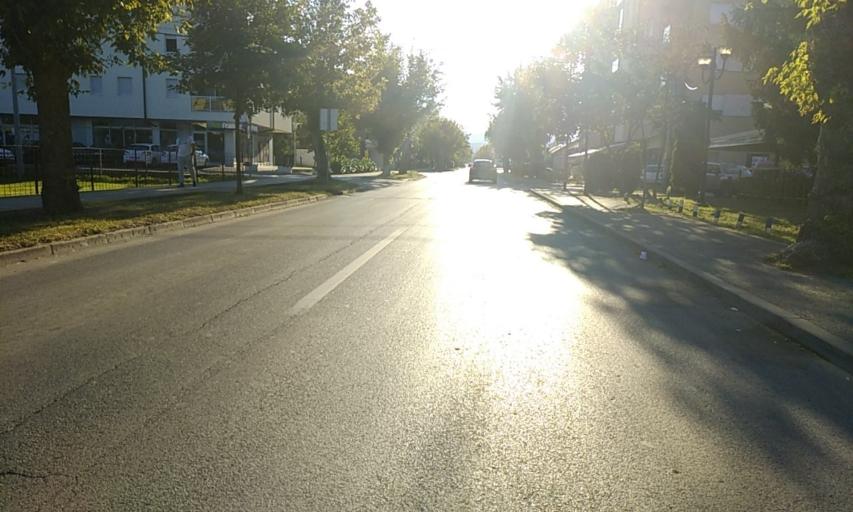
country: BA
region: Republika Srpska
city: Starcevica
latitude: 44.7658
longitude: 17.2054
